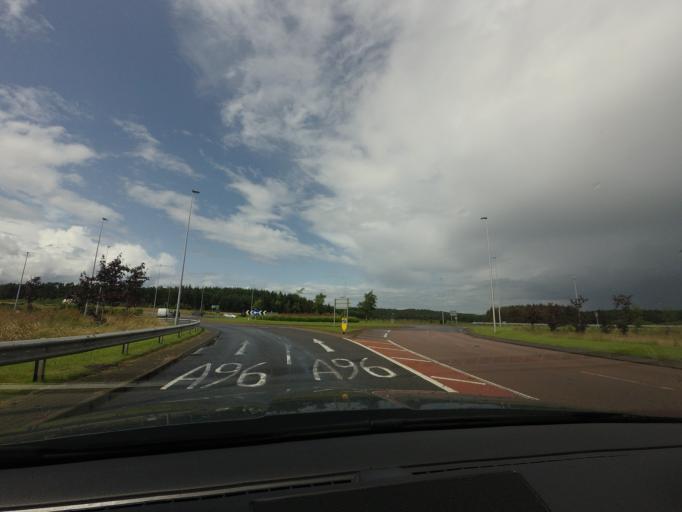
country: GB
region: Scotland
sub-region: Moray
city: Fochabers
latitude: 57.6260
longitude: -3.1416
